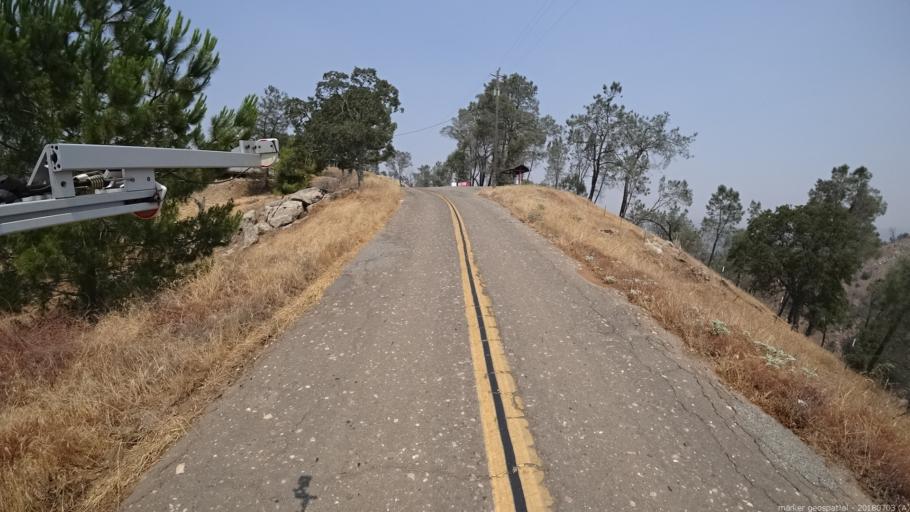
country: US
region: California
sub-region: Fresno County
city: Auberry
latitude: 37.0533
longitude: -119.6479
